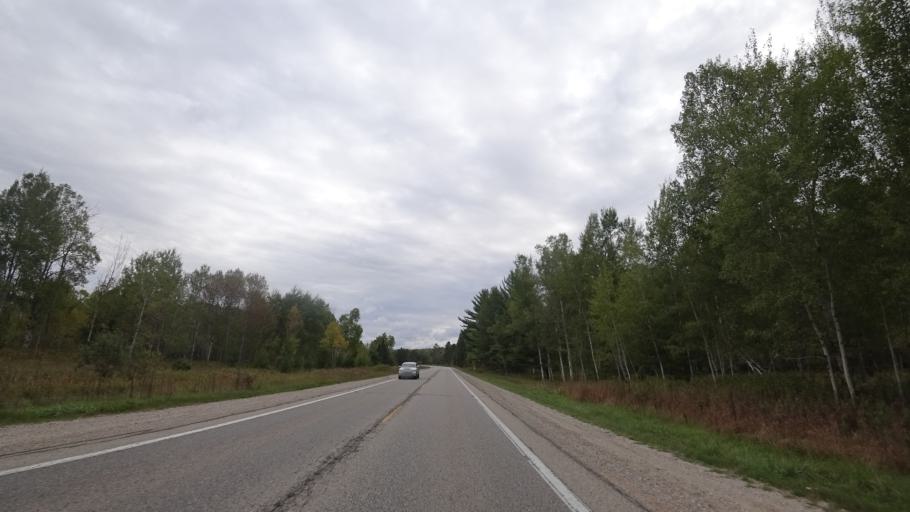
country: US
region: Michigan
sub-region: Charlevoix County
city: Boyne City
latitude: 45.2174
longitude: -84.9241
